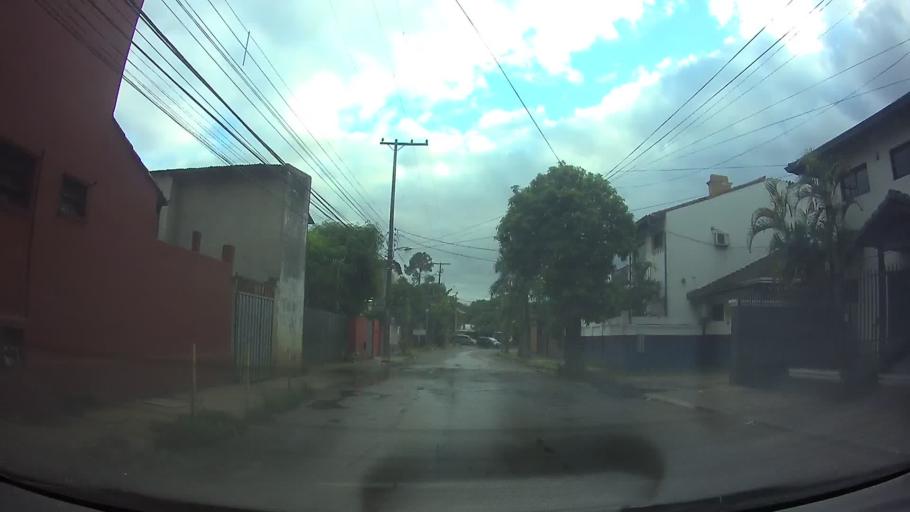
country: PY
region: Central
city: Fernando de la Mora
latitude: -25.3134
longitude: -57.5535
